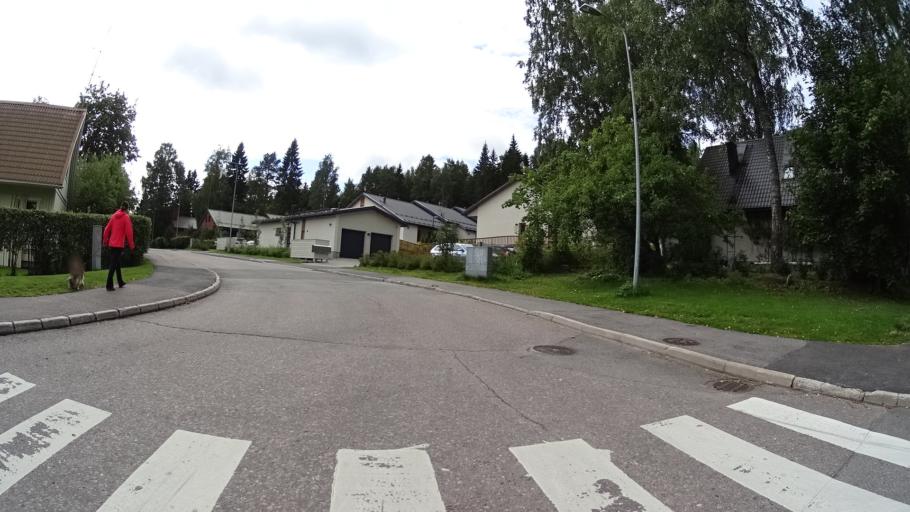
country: FI
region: Uusimaa
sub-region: Helsinki
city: Helsinki
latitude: 60.2525
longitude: 24.9289
